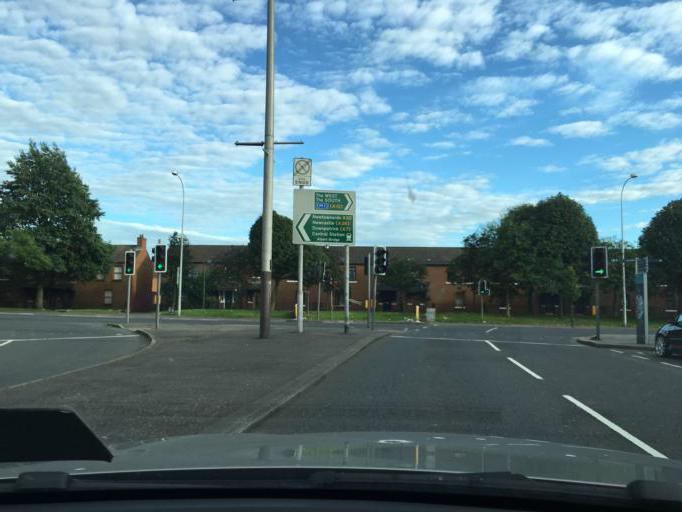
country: GB
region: Northern Ireland
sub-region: City of Belfast
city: Belfast
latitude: 54.5958
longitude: -5.9212
